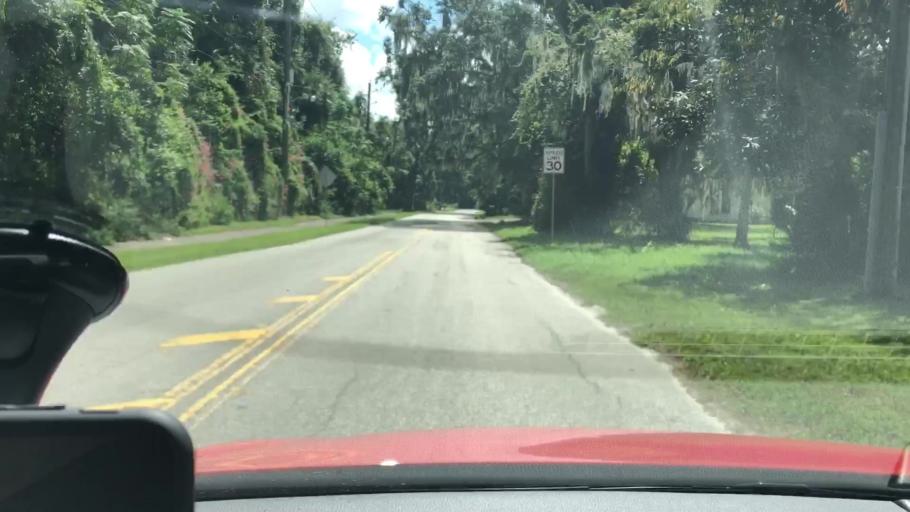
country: US
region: Florida
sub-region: Volusia County
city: New Smyrna Beach
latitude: 29.0188
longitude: -80.9285
